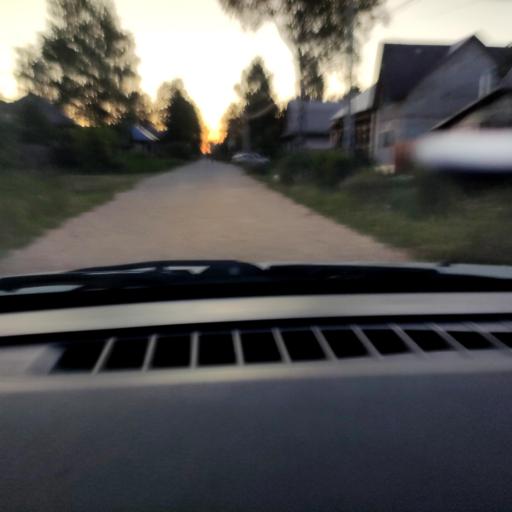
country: RU
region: Perm
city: Perm
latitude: 58.0230
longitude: 56.3273
